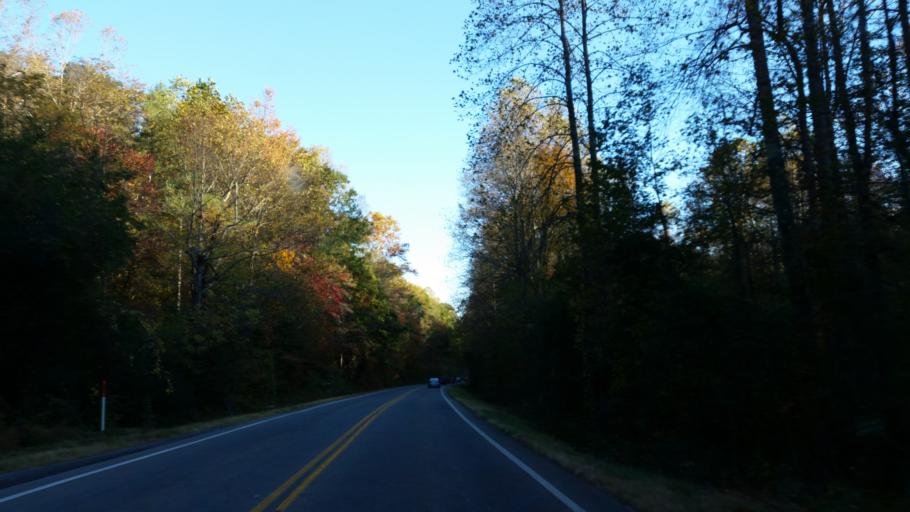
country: US
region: Georgia
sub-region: Pickens County
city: Jasper
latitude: 34.5601
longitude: -84.2995
